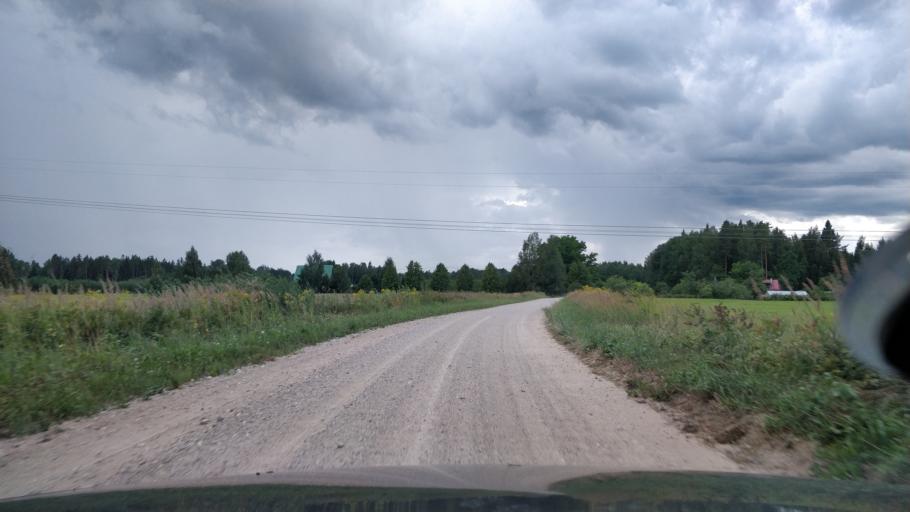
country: LV
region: Ogre
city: Ogre
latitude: 56.8034
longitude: 24.6835
